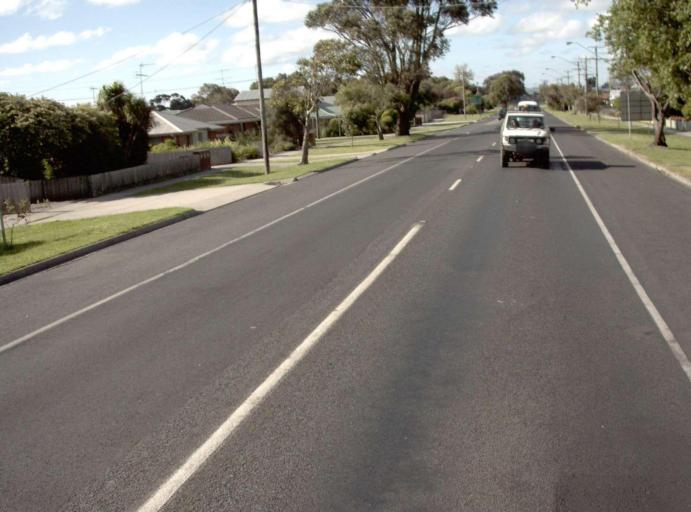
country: AU
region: Victoria
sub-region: Bass Coast
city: North Wonthaggi
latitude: -38.6013
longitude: 145.5930
